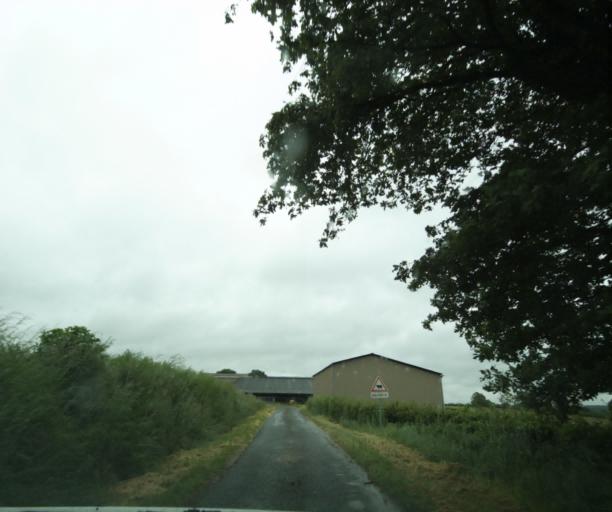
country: FR
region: Bourgogne
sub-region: Departement de Saone-et-Loire
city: Palinges
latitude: 46.5612
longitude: 4.2031
